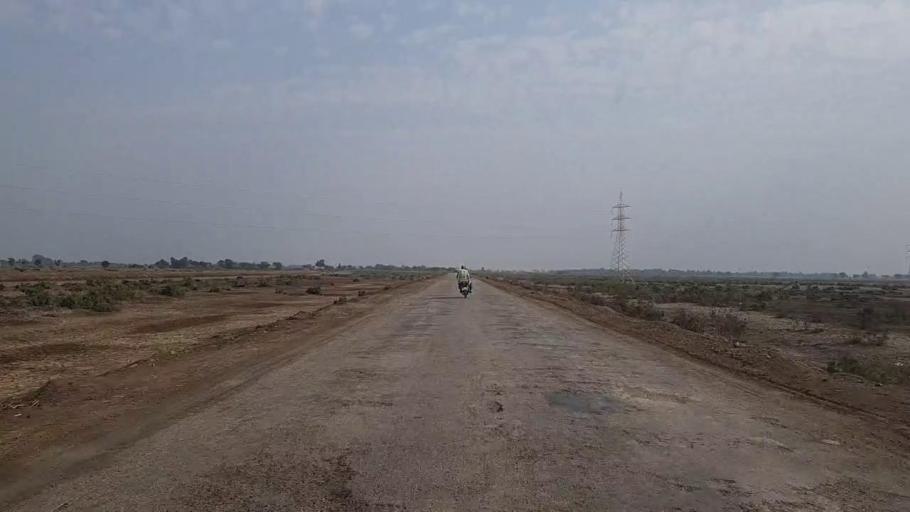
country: PK
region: Sindh
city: Mirpur Khas
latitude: 25.4205
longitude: 69.0264
